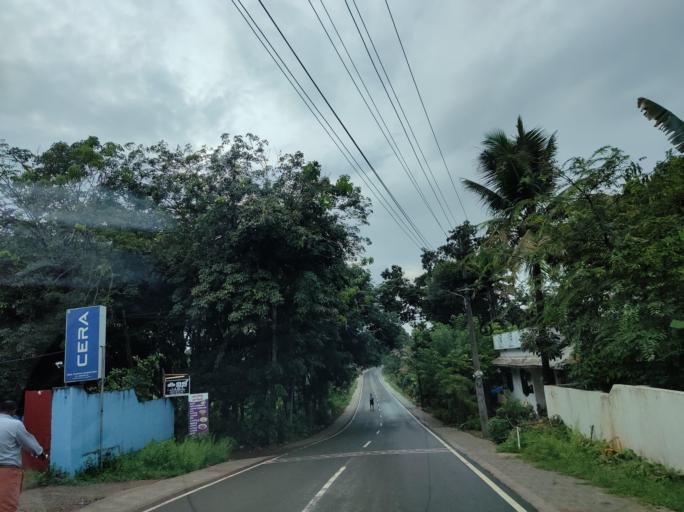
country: IN
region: Kerala
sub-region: Alappuzha
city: Mavelikara
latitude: 9.2273
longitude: 76.5750
